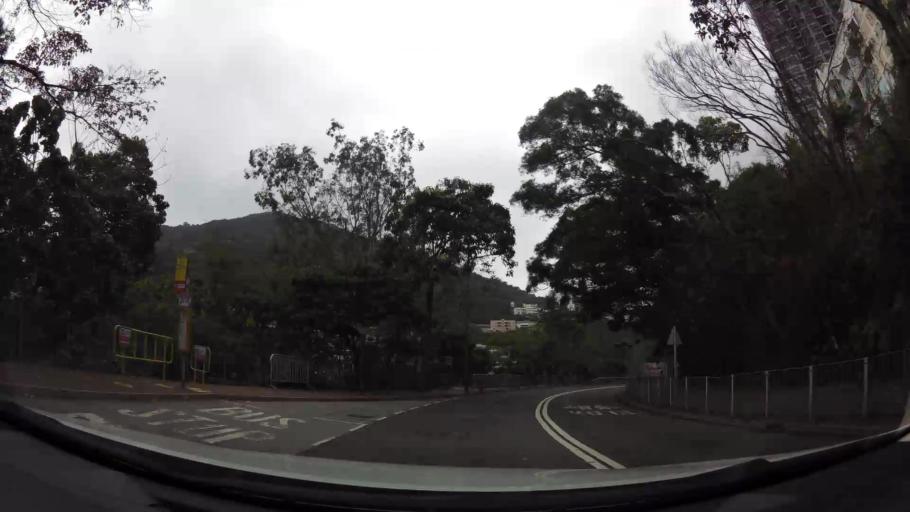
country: HK
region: Central and Western
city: Central
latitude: 22.2704
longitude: 114.1255
